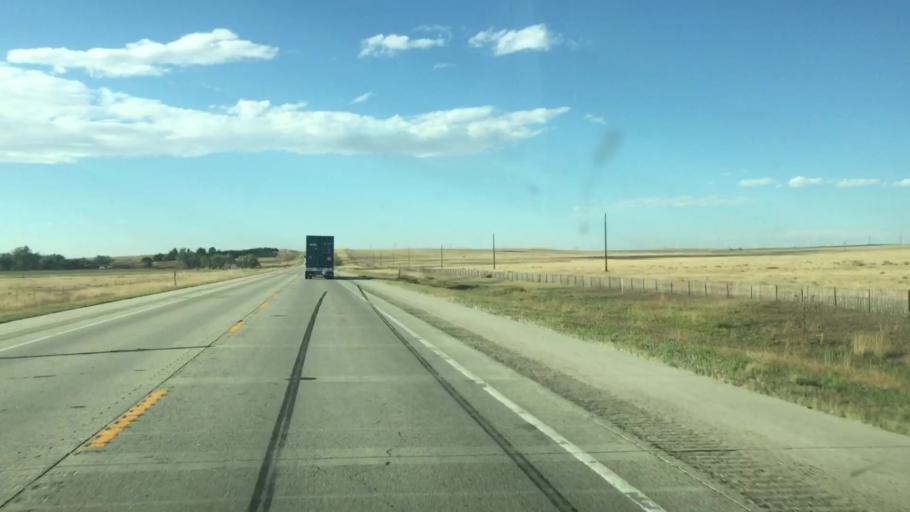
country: US
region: Colorado
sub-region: Lincoln County
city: Limon
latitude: 39.2346
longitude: -103.6199
